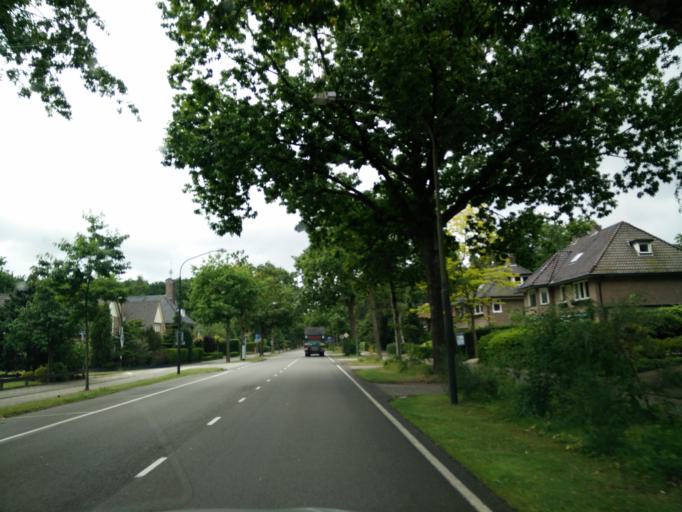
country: NL
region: Gelderland
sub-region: Gemeente Apeldoorn
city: Apeldoorn
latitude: 52.2145
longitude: 5.9326
